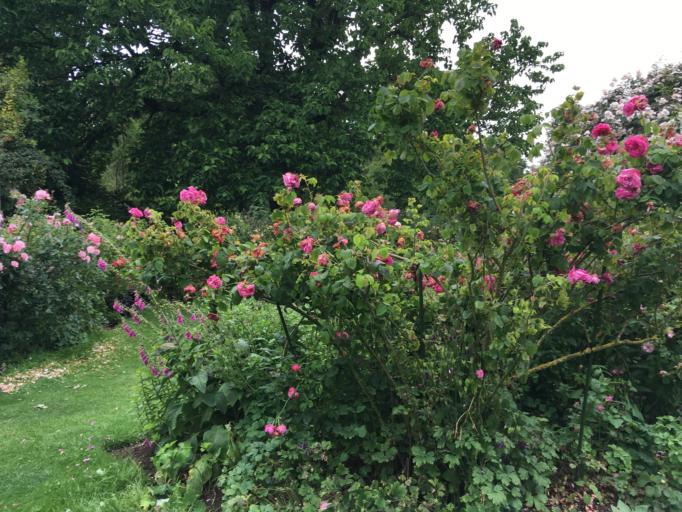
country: NZ
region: Canterbury
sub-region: Christchurch City
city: Christchurch
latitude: -43.5332
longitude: 172.6231
